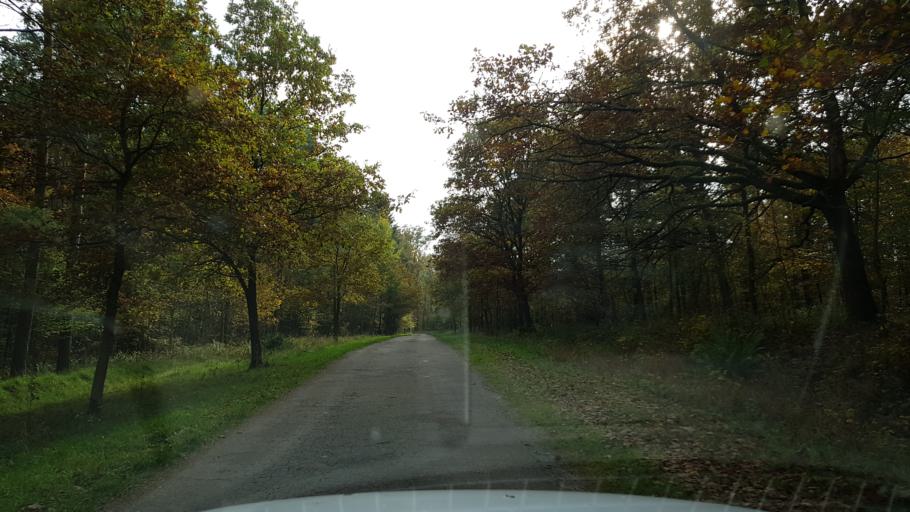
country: PL
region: West Pomeranian Voivodeship
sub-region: Powiat lobeski
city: Wegorzyno
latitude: 53.5098
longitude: 15.4960
